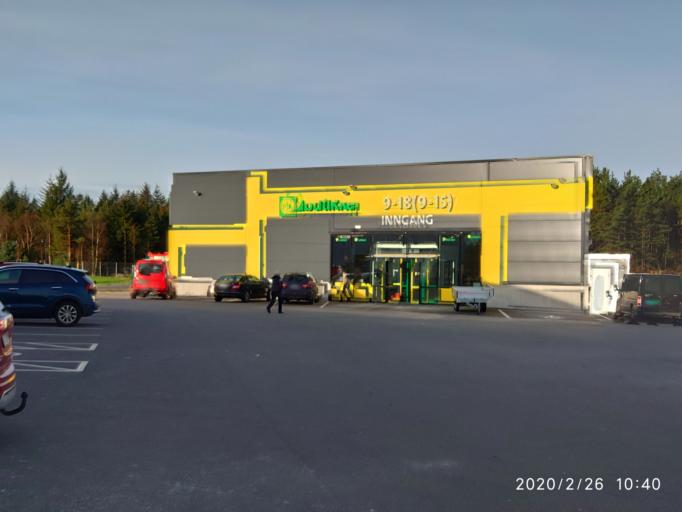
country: NO
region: Hordaland
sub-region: Stord
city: Leirvik
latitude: 59.7638
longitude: 5.4488
